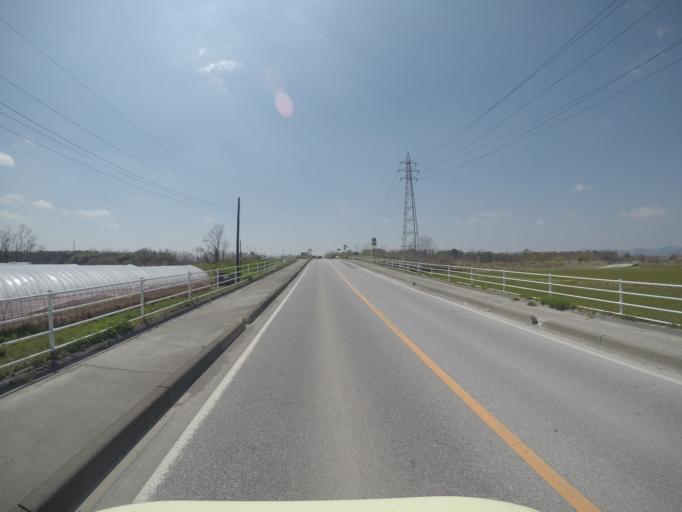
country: JP
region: Tochigi
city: Mibu
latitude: 36.4376
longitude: 139.7722
